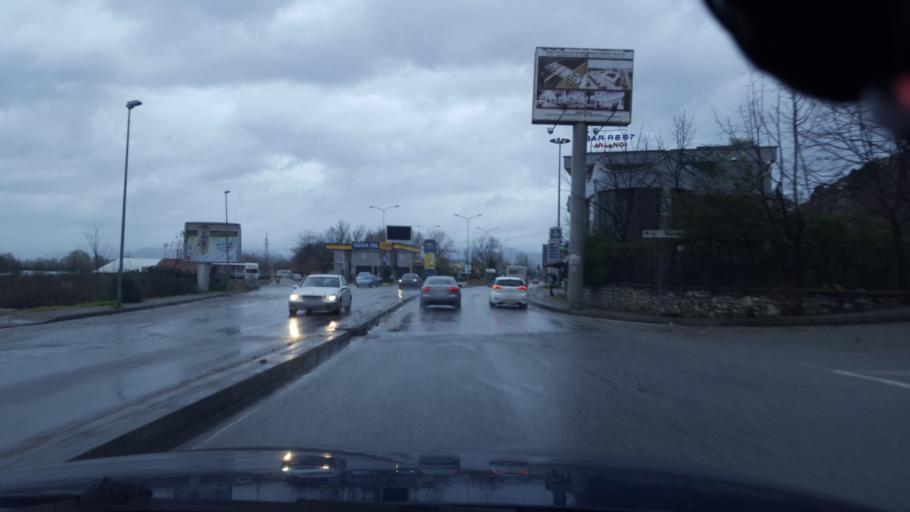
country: AL
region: Shkoder
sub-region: Rrethi i Shkodres
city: Shkoder
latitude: 42.0478
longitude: 19.4919
